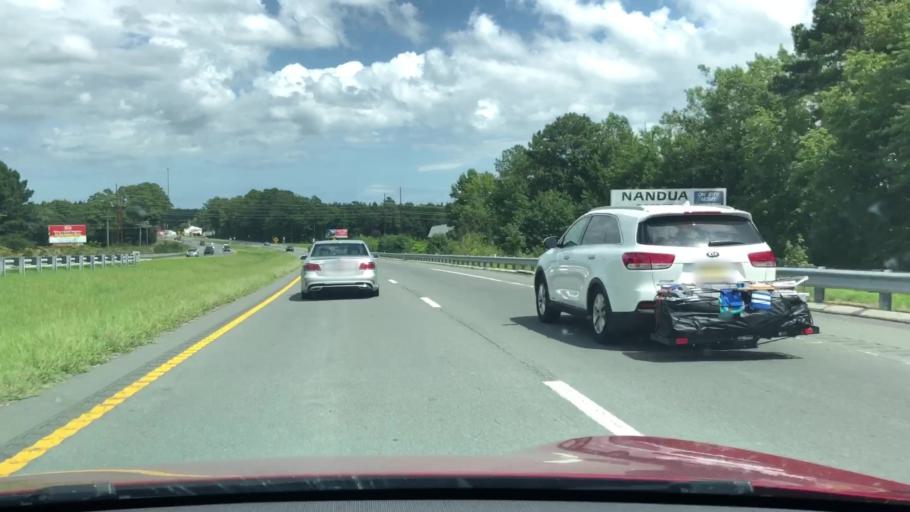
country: US
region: Virginia
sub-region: Accomack County
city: Accomac
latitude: 37.7026
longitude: -75.7055
